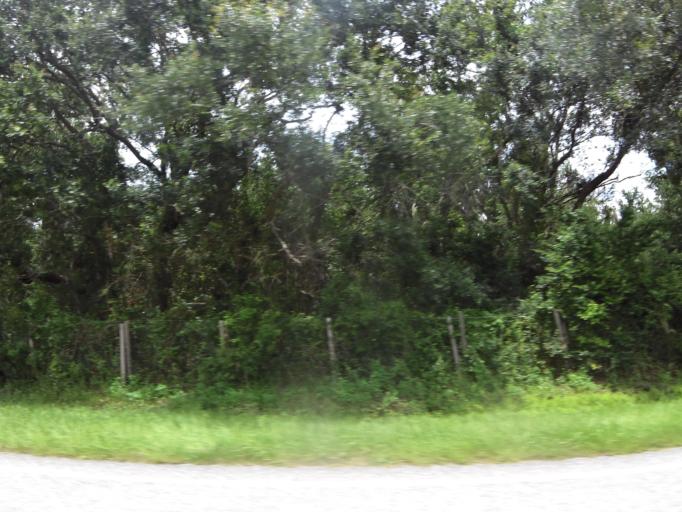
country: US
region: Florida
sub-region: Putnam County
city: East Palatka
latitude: 29.6773
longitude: -81.4574
